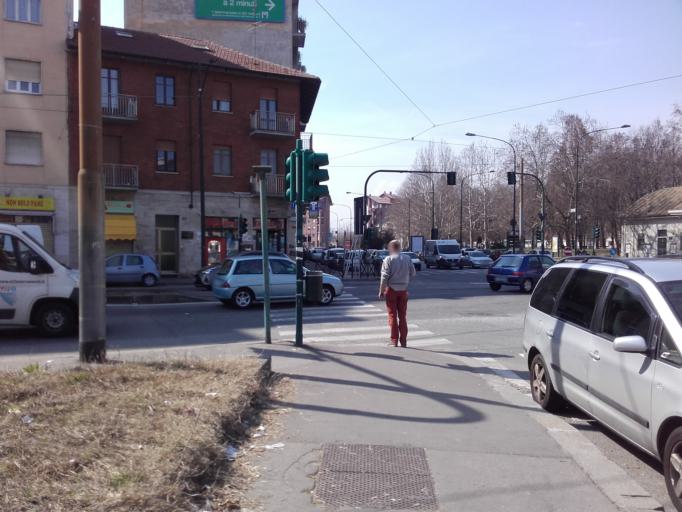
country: IT
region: Piedmont
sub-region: Provincia di Torino
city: Venaria Reale
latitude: 45.1117
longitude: 7.6604
